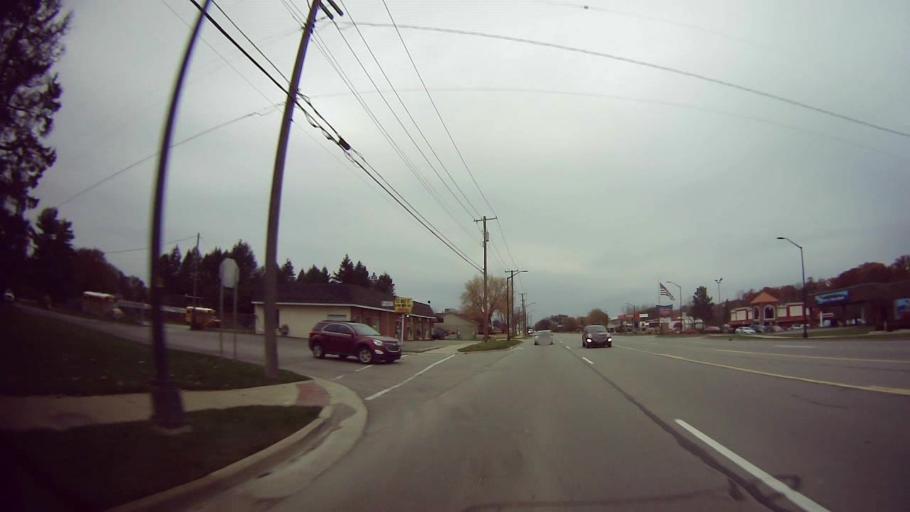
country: US
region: Michigan
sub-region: Oakland County
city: Waterford
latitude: 42.7140
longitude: -83.4112
